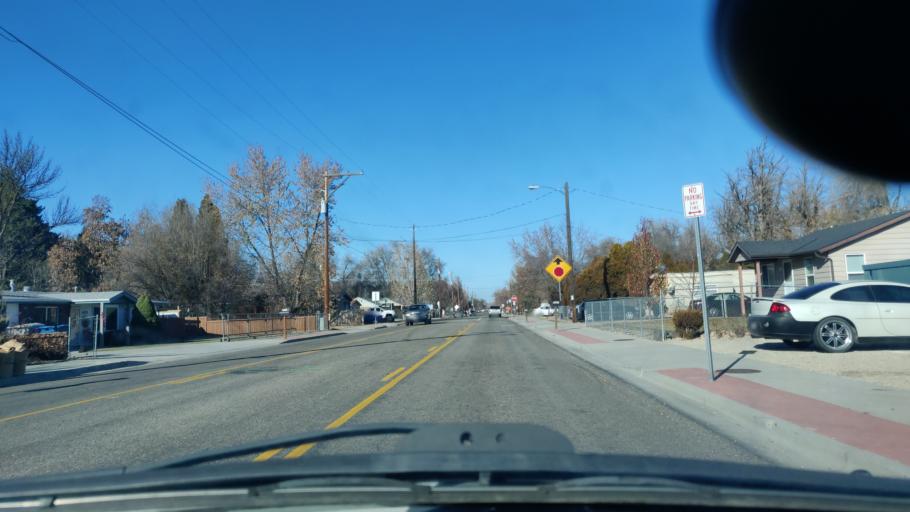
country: US
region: Idaho
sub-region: Ada County
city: Garden City
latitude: 43.6363
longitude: -116.2495
